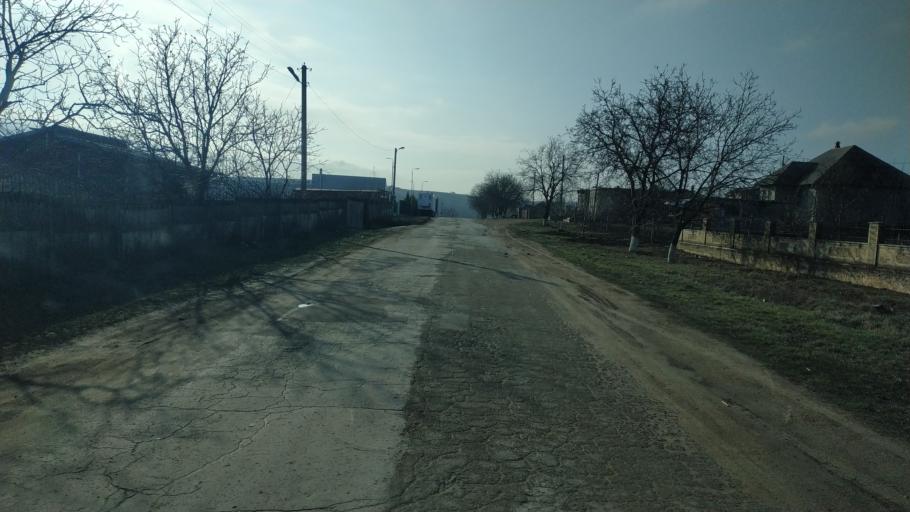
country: MD
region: Laloveni
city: Ialoveni
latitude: 46.9464
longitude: 28.7216
